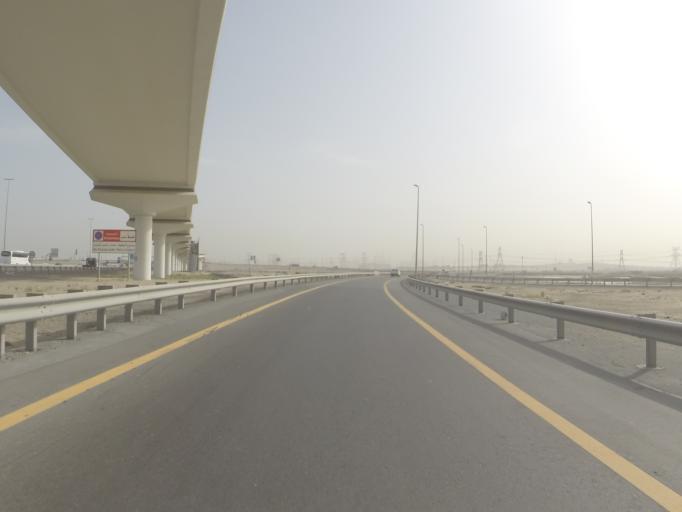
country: AE
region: Dubai
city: Dubai
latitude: 25.0120
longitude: 55.0975
